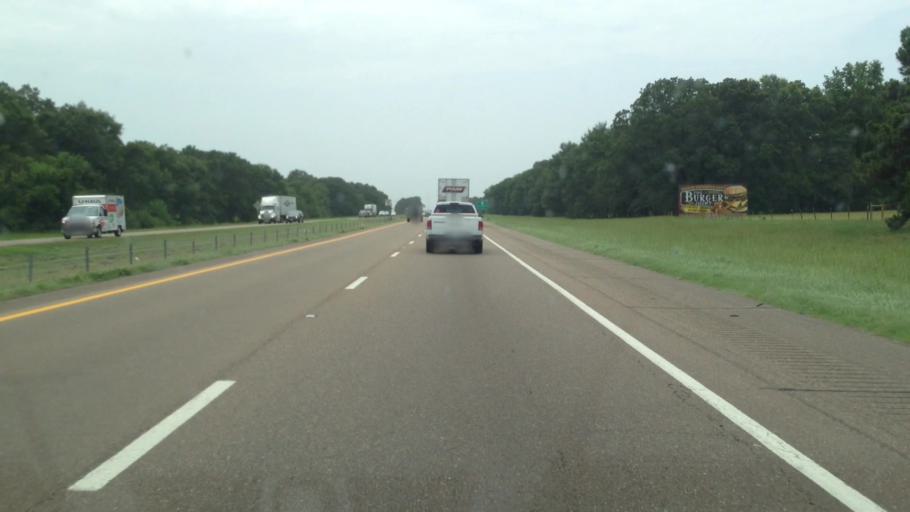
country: US
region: Texas
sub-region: Bowie County
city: New Boston
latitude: 33.4722
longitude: -94.3834
